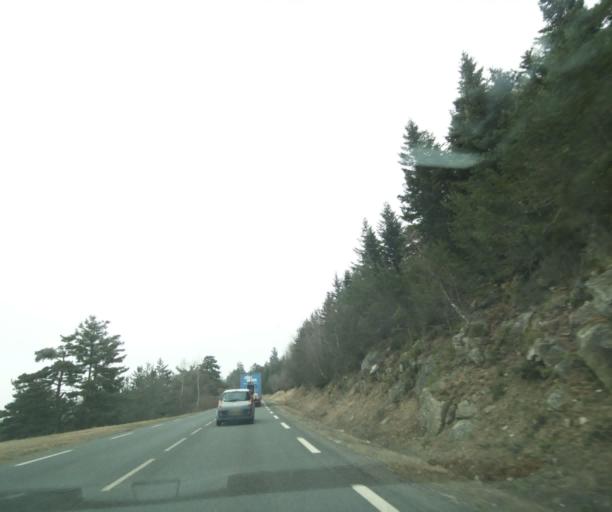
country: FR
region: Languedoc-Roussillon
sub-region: Departement de la Lozere
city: Langogne
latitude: 44.6884
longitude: 3.8093
